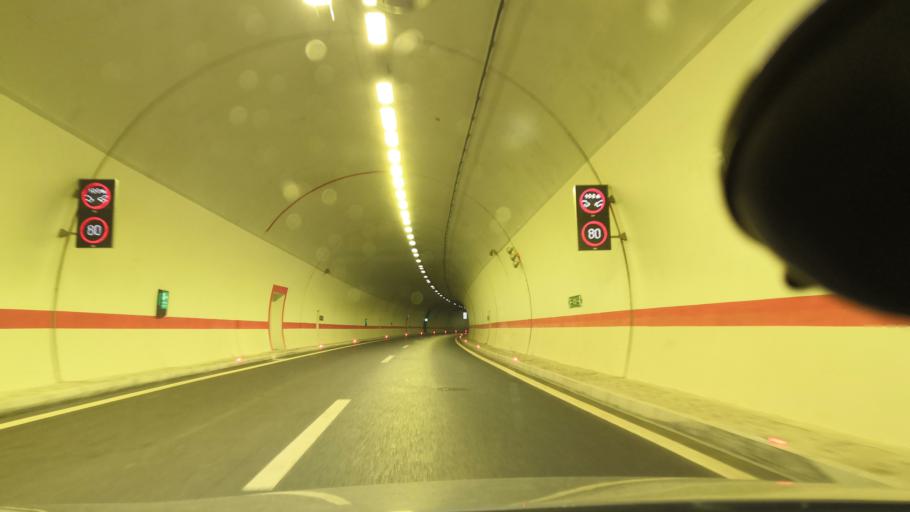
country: RS
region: Central Serbia
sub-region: Pcinjski Okrug
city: Vladicin Han
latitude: 42.7313
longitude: 22.0735
